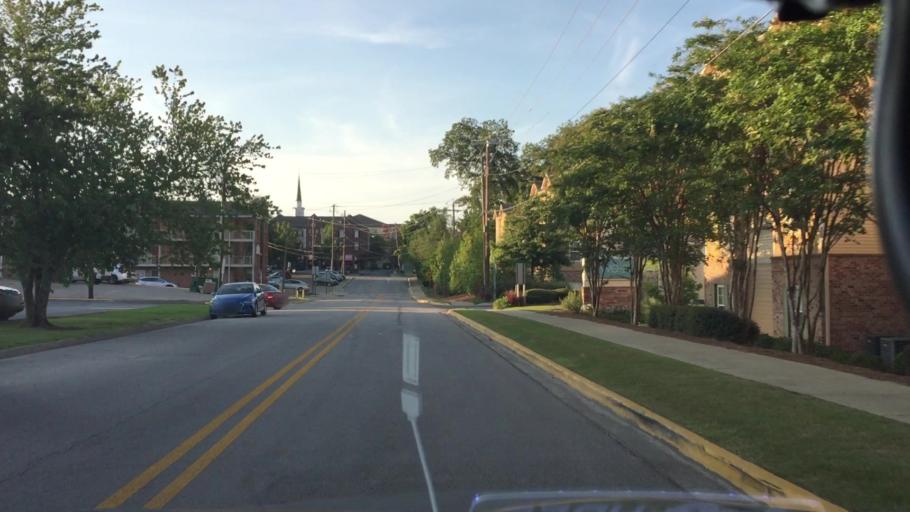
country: US
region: Alabama
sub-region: Lee County
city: Auburn
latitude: 32.6025
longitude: -85.4786
